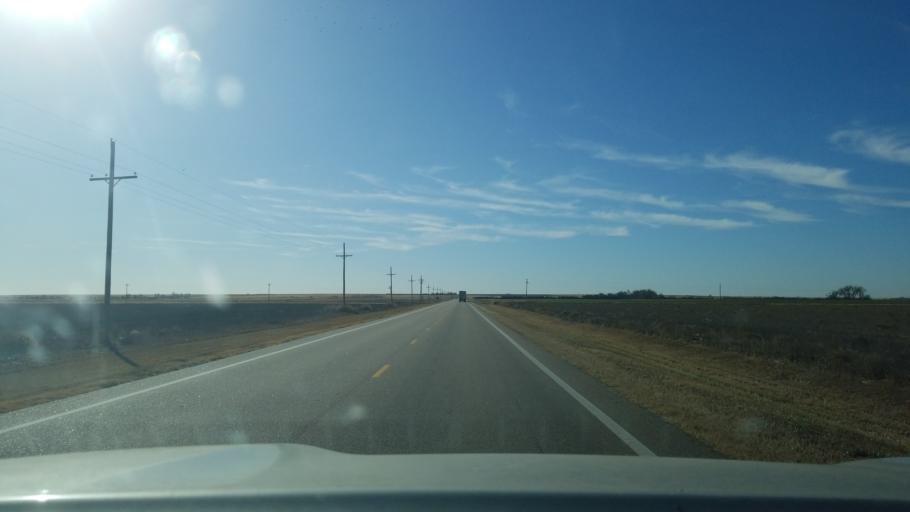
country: US
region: Kansas
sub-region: Ness County
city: Ness City
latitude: 38.4242
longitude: -99.8986
